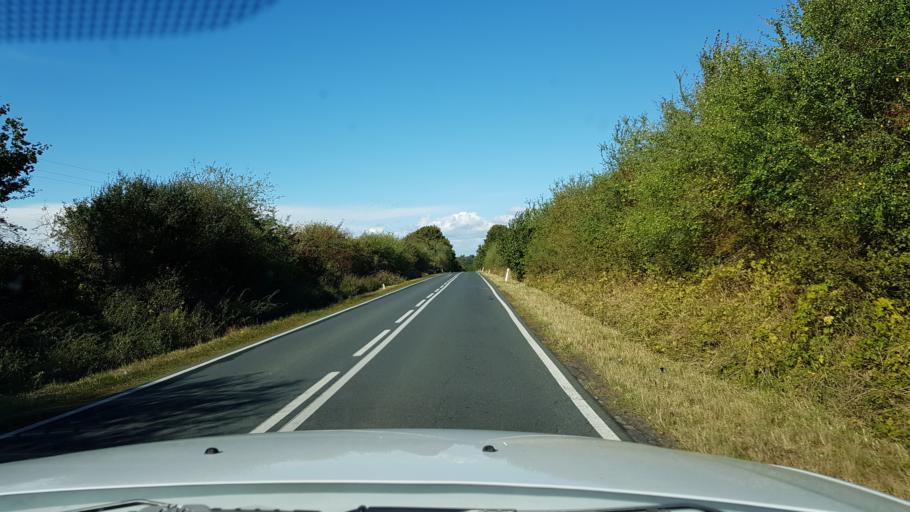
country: PL
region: West Pomeranian Voivodeship
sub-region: Powiat gryfinski
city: Banie
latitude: 53.1477
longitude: 14.6073
